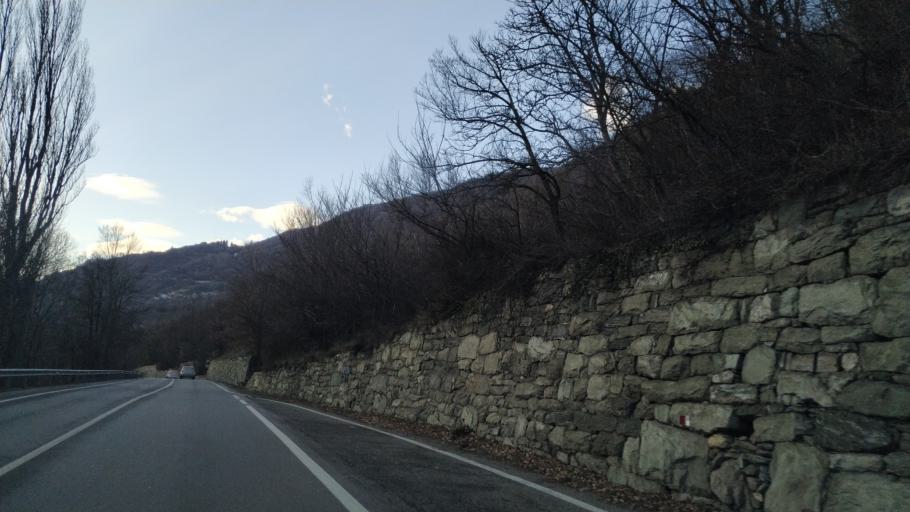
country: IT
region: Aosta Valley
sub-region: Valle d'Aosta
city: Chez Croiset
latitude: 45.7460
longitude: 7.4995
